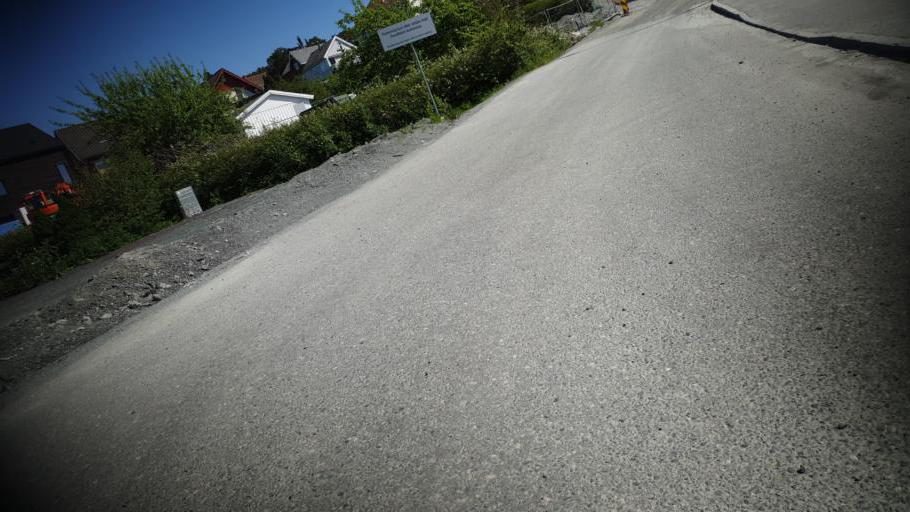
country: NO
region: Sor-Trondelag
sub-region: Klaebu
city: Klaebu
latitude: 63.4284
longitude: 10.5391
